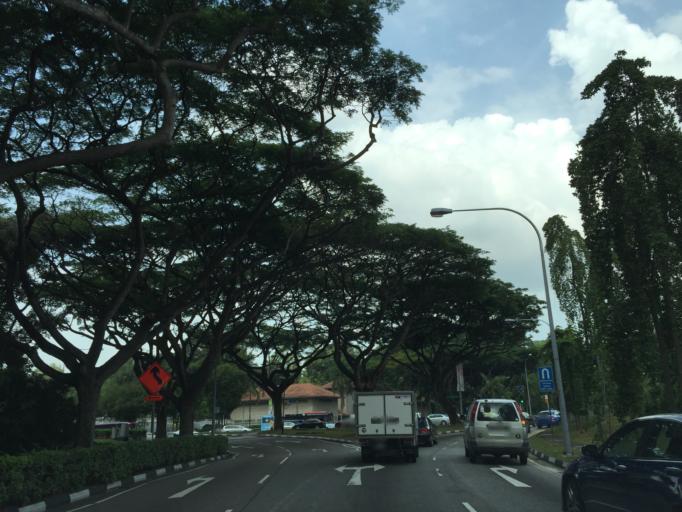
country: SG
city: Singapore
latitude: 1.3112
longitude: 103.8448
